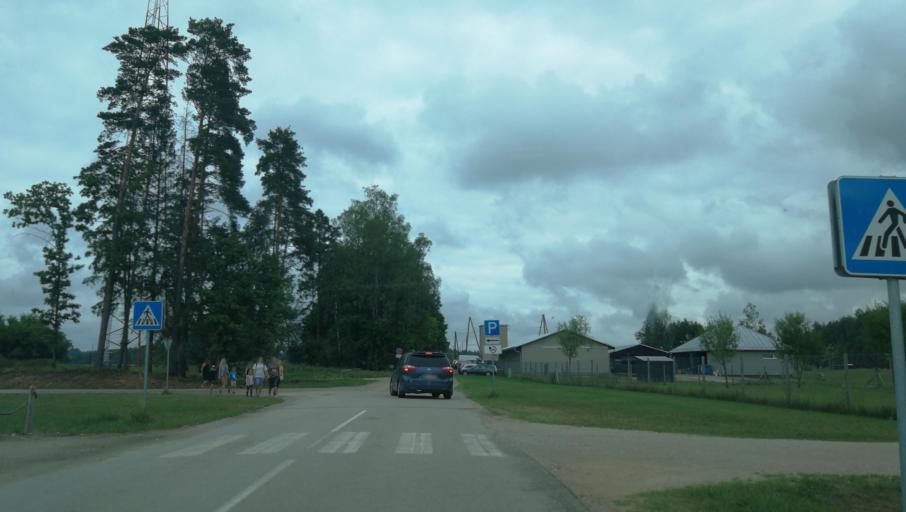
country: LV
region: Ogre
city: Jumprava
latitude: 56.7842
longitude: 25.0162
